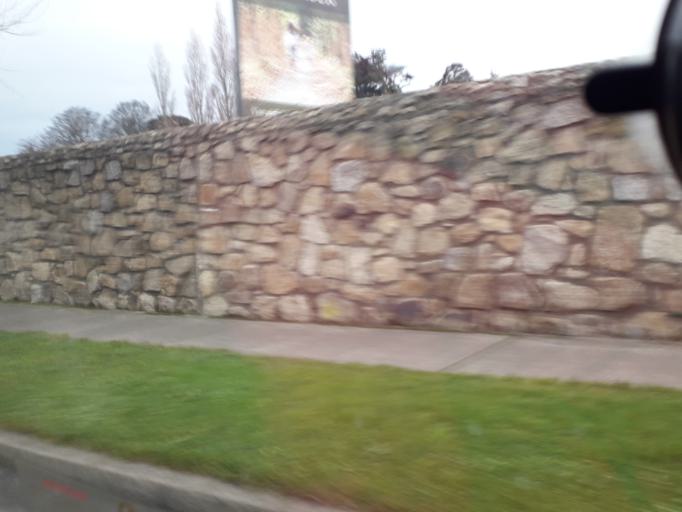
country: IE
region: Leinster
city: Balally
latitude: 53.2886
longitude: -6.2369
